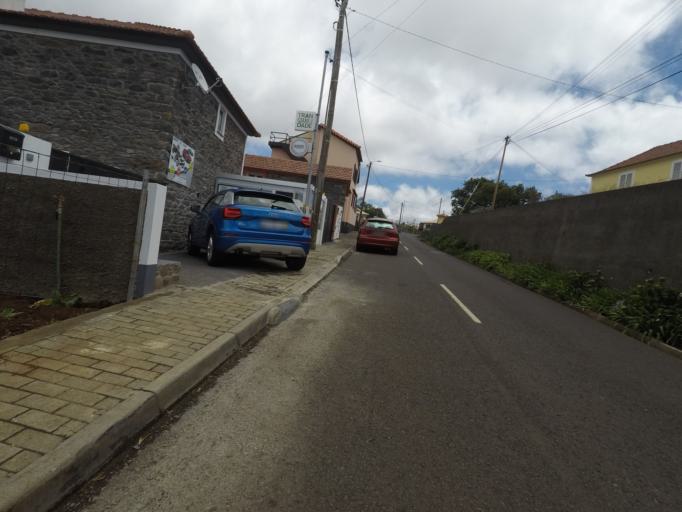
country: PT
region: Madeira
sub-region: Calheta
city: Estreito da Calheta
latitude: 32.7537
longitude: -17.2068
